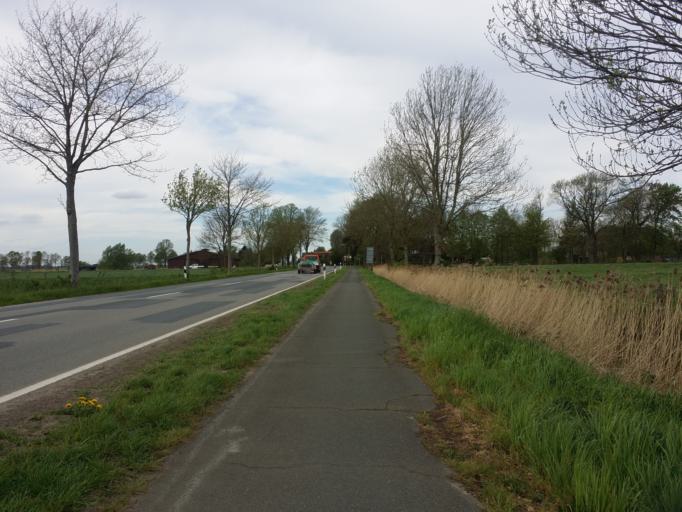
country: DE
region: Lower Saxony
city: Lemwerder
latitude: 53.1450
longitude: 8.5557
